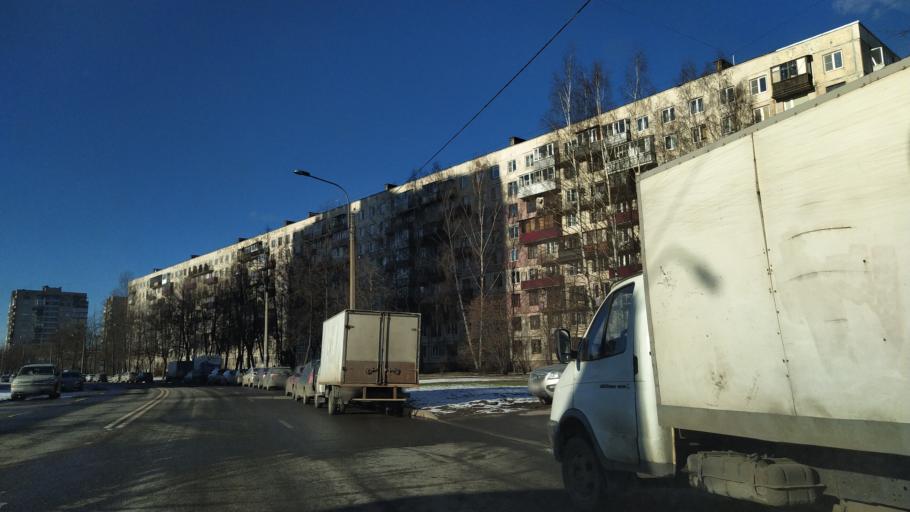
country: RU
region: Leningrad
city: Kalininskiy
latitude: 59.9710
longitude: 30.4220
